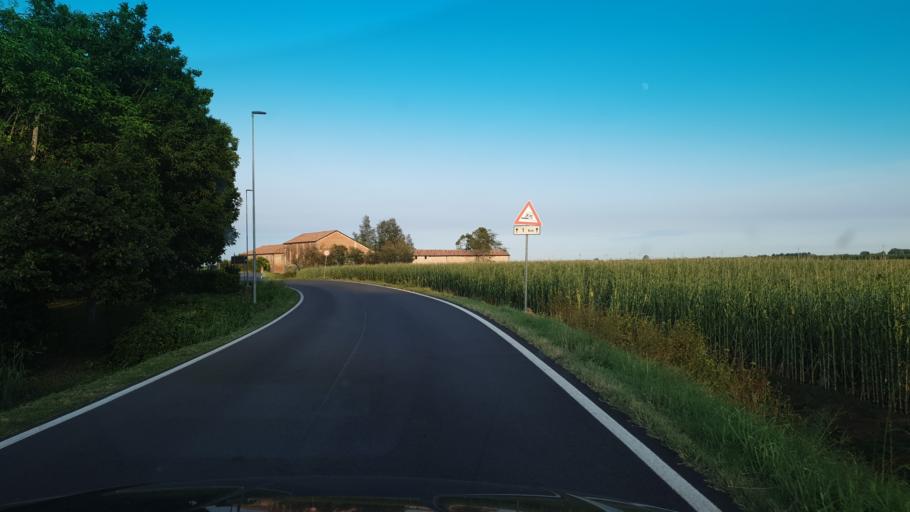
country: IT
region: Veneto
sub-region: Provincia di Rovigo
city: Castelguglielmo
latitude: 45.0306
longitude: 11.5553
